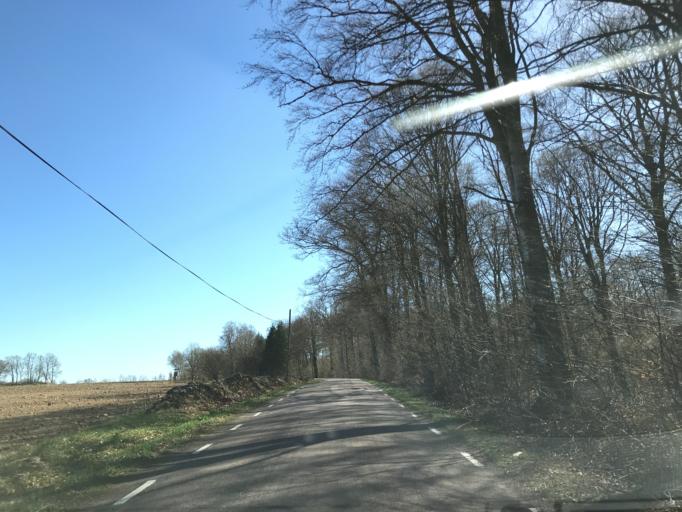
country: SE
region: Skane
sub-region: Svalovs Kommun
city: Kagerod
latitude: 56.0012
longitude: 13.1631
